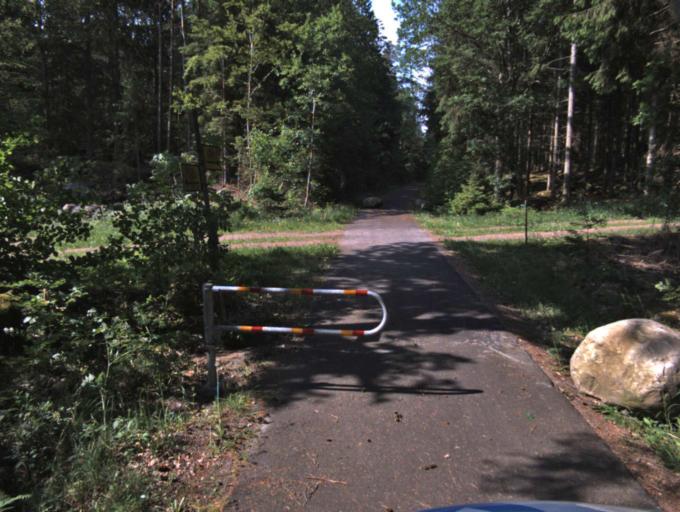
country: SE
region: Skane
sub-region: Kristianstads Kommun
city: Tollarp
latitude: 56.1978
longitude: 14.2588
